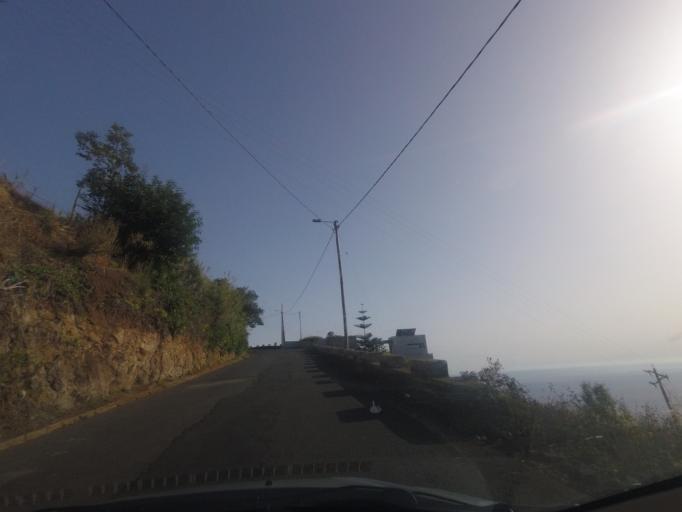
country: PT
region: Madeira
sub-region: Calheta
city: Arco da Calheta
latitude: 32.7053
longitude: -17.1262
